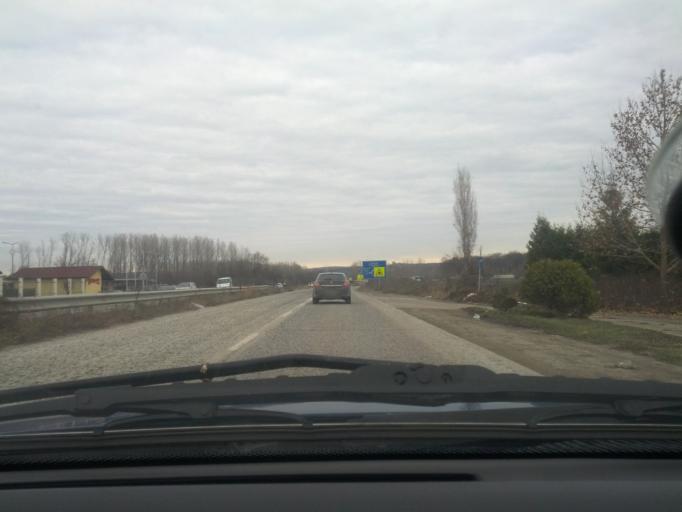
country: BG
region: Vratsa
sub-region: Obshtina Vratsa
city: Vratsa
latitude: 43.2392
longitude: 23.5667
